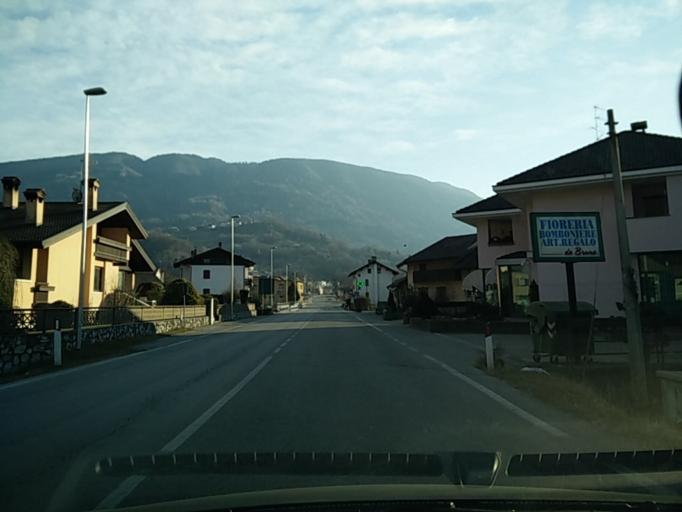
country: IT
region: Veneto
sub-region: Provincia di Belluno
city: Farra d'Alpago
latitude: 46.1229
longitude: 12.3559
